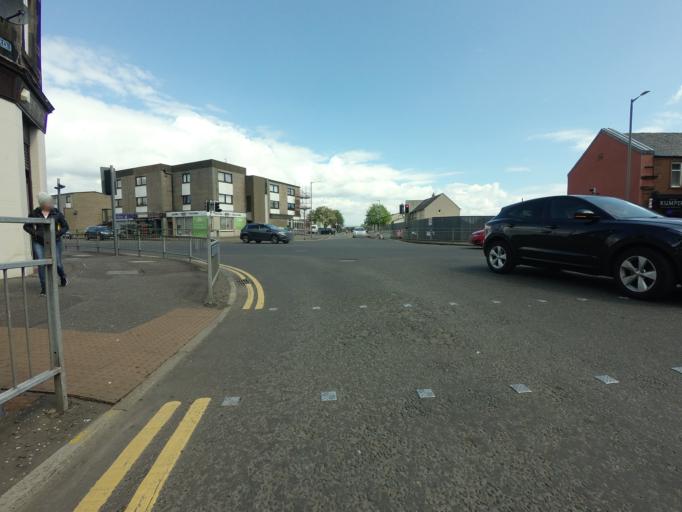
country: GB
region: Scotland
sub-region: Falkirk
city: Falkirk
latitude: 56.0137
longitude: -3.7896
